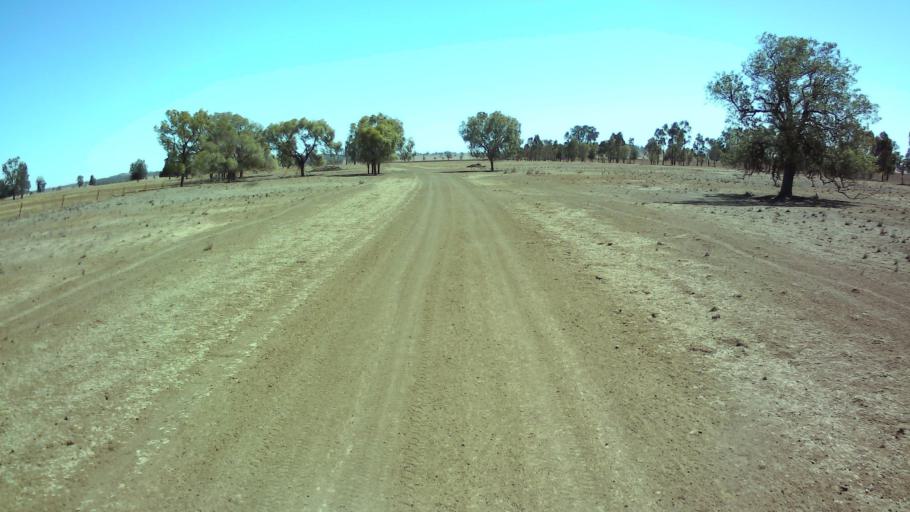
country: AU
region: New South Wales
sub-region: Forbes
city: Forbes
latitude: -33.7160
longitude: 147.6668
